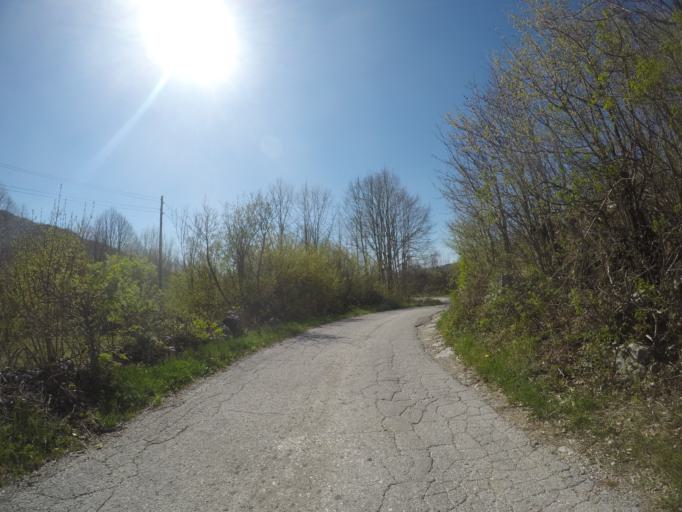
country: ME
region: Danilovgrad
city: Danilovgrad
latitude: 42.5381
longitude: 19.0117
